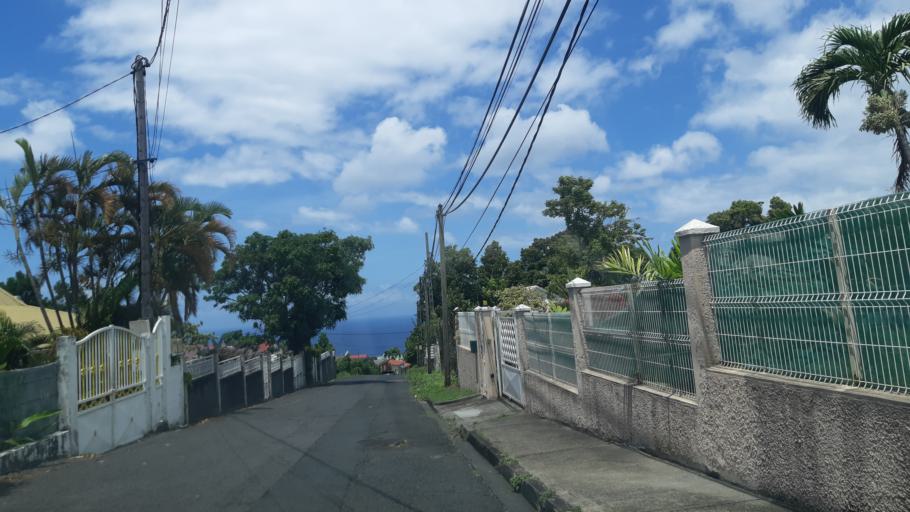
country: GP
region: Guadeloupe
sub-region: Guadeloupe
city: Saint-Claude
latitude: 16.0110
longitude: -61.7123
